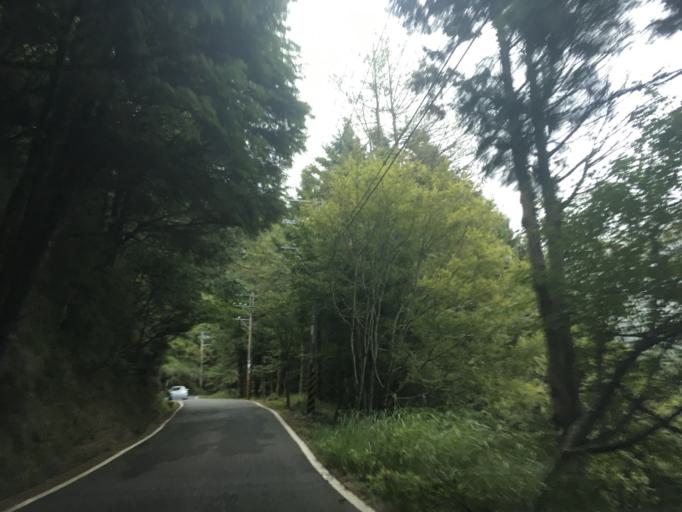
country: TW
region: Taiwan
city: Fengyuan
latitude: 24.2692
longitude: 121.0220
